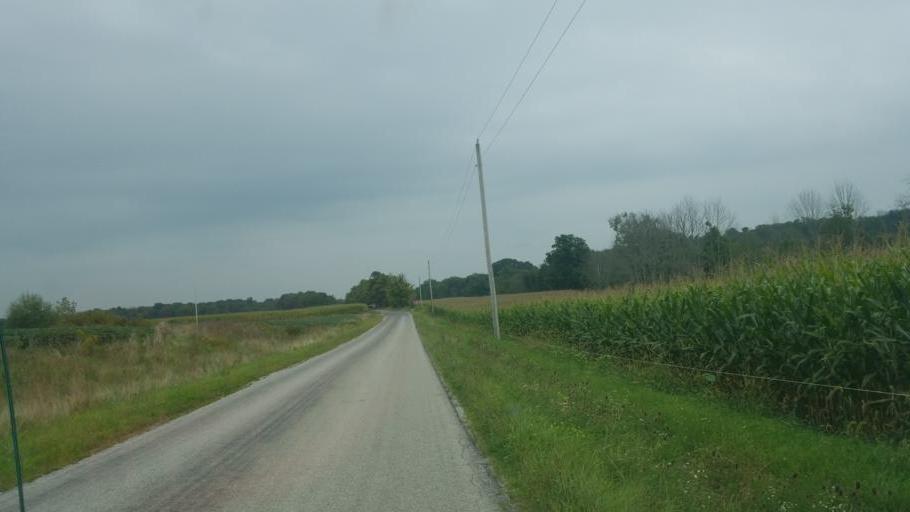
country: US
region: Ohio
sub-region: Wayne County
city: Creston
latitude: 40.9587
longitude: -81.9597
